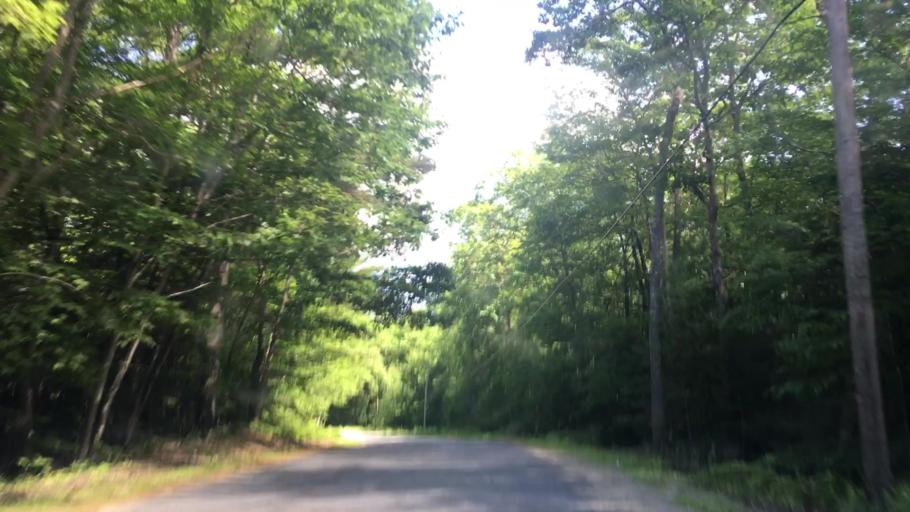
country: US
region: Maine
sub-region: Franklin County
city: Chesterville
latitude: 44.5592
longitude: -70.1272
